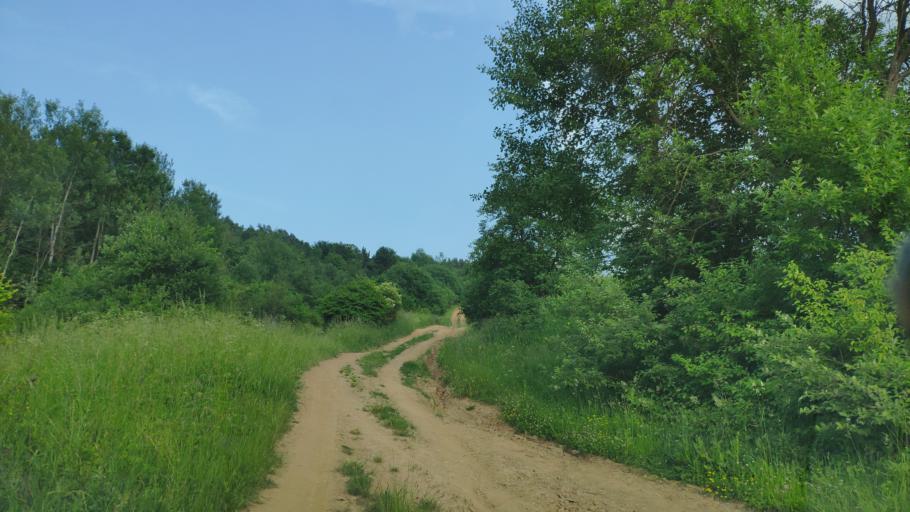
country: SK
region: Presovsky
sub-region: Okres Presov
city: Presov
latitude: 48.9561
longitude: 21.1208
